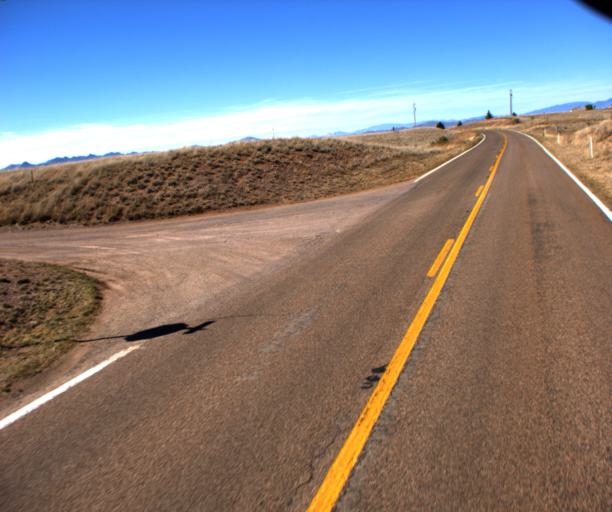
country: US
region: Arizona
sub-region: Cochise County
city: Huachuca City
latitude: 31.6615
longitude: -110.6049
